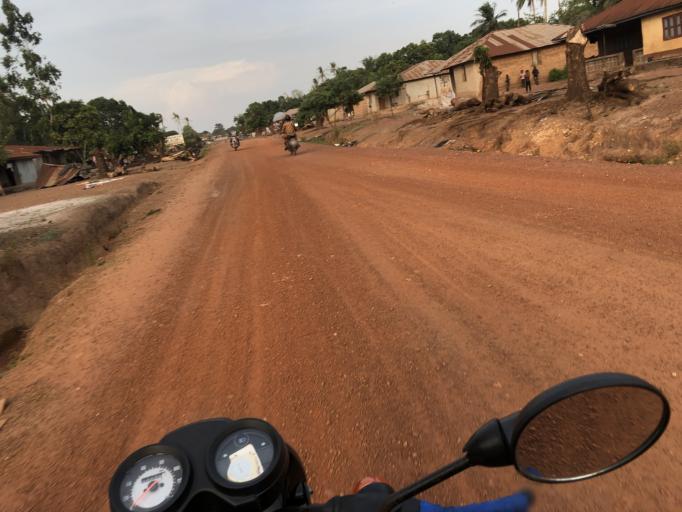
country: SL
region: Northern Province
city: Yonibana
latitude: 8.4683
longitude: -12.2044
